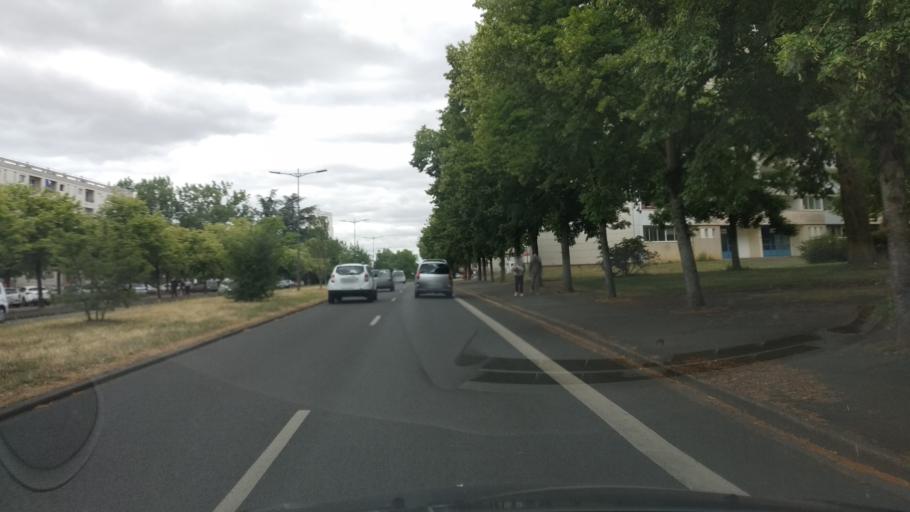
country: FR
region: Poitou-Charentes
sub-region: Departement de la Vienne
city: Poitiers
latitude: 46.5904
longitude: 0.3541
